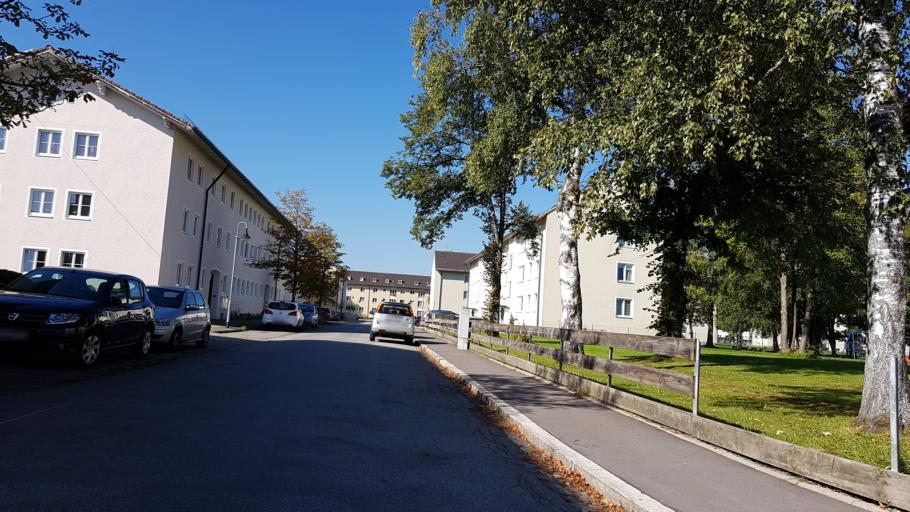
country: DE
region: Bavaria
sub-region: Swabia
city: Fuessen
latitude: 47.5718
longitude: 10.6803
